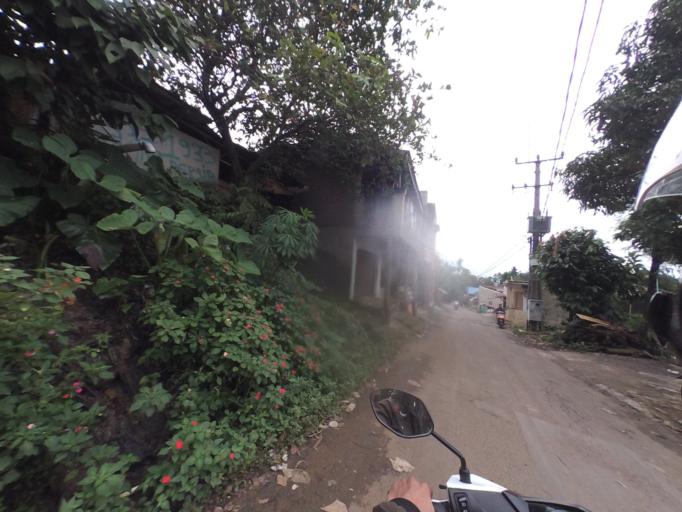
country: ID
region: West Java
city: Bogor
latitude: -6.6250
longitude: 106.7461
